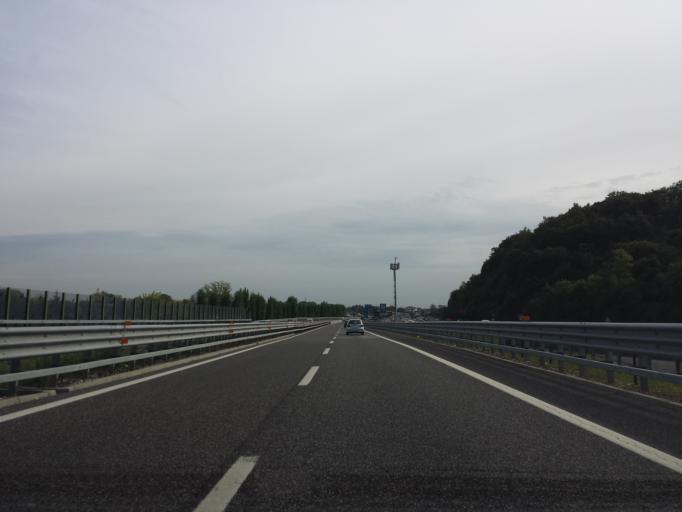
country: IT
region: Veneto
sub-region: Provincia di Vicenza
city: Arcugnano-Torri
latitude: 45.5160
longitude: 11.5524
